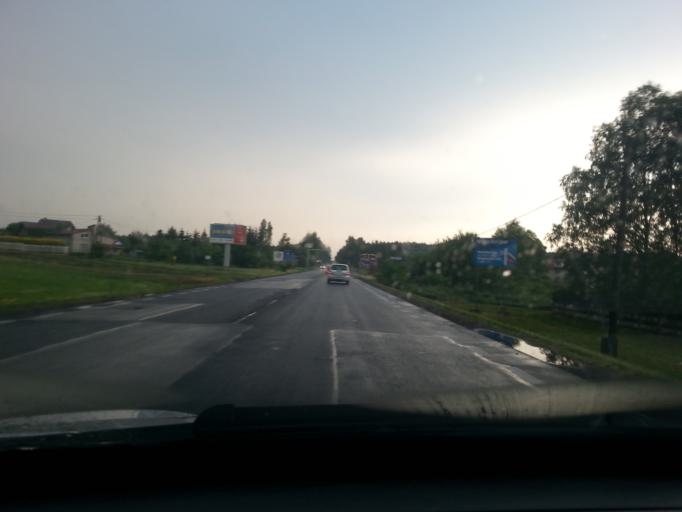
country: PL
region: Lodz Voivodeship
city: Lodz
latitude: 51.8264
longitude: 19.5231
